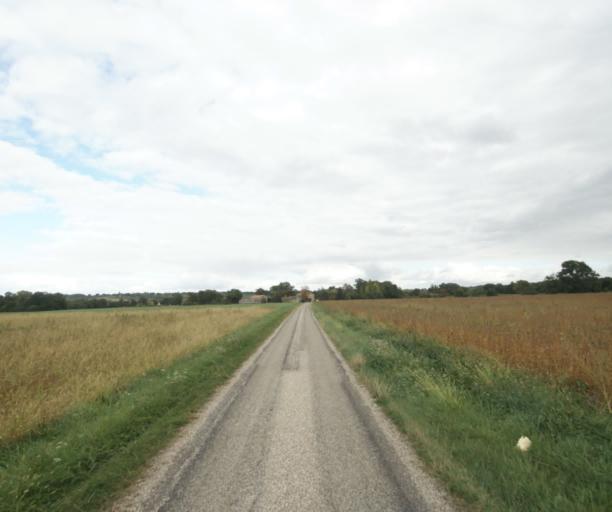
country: FR
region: Midi-Pyrenees
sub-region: Departement du Gers
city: Eauze
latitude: 43.9276
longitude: 0.1303
